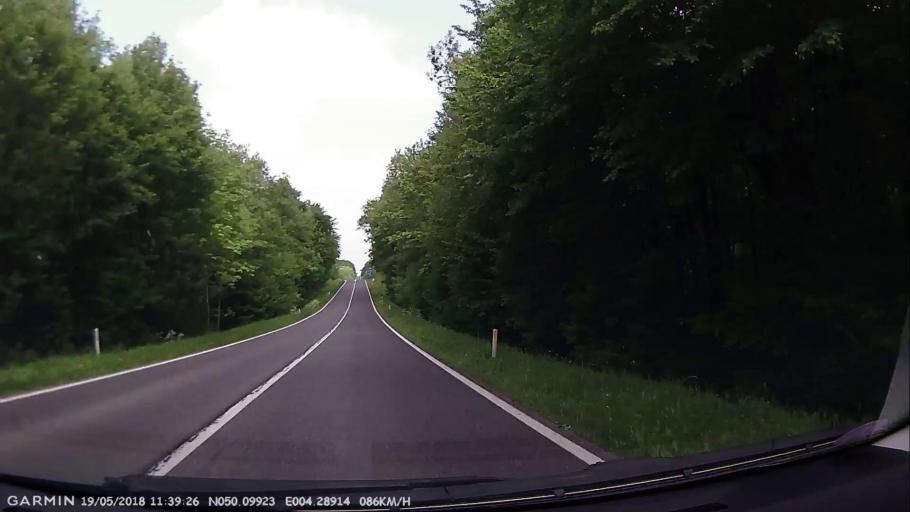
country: BE
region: Wallonia
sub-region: Province du Hainaut
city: Chimay
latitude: 50.0996
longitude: 4.2890
